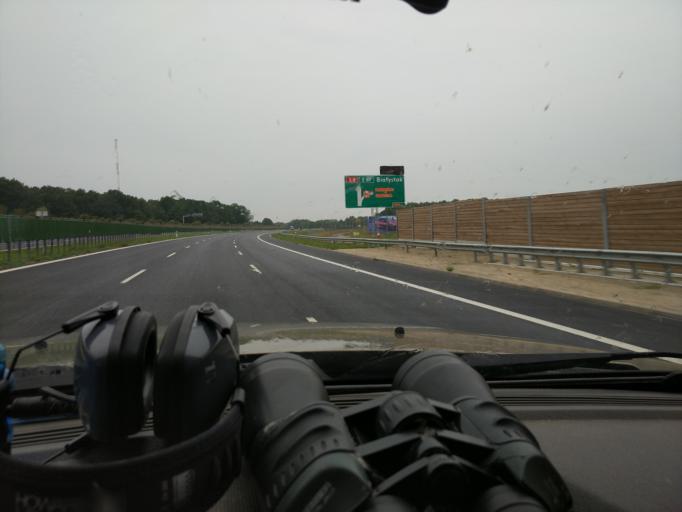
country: PL
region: Masovian Voivodeship
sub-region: Powiat wolominski
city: Slupno
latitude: 52.3451
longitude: 21.1564
